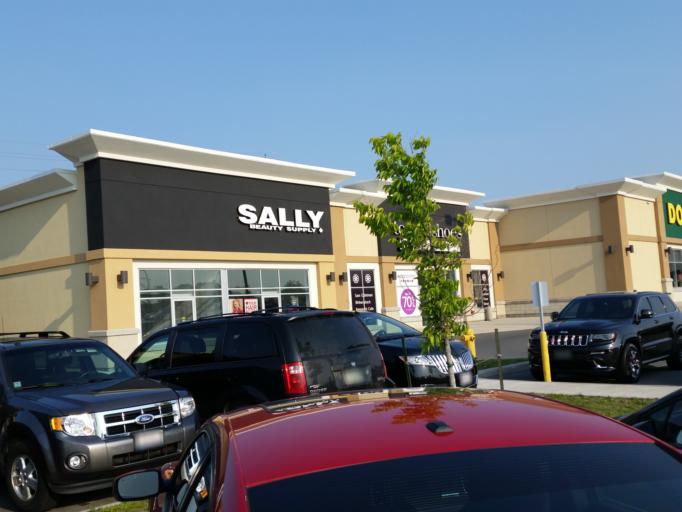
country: CA
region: Ontario
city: Greater Sudbury
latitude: 46.5014
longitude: -80.9453
